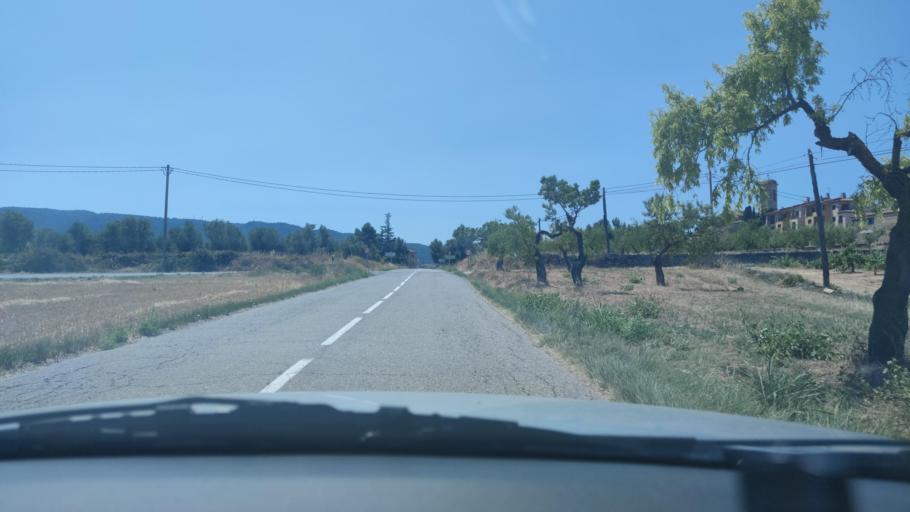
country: ES
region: Catalonia
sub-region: Provincia de Tarragona
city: Vallclara
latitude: 41.3858
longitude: 0.9489
